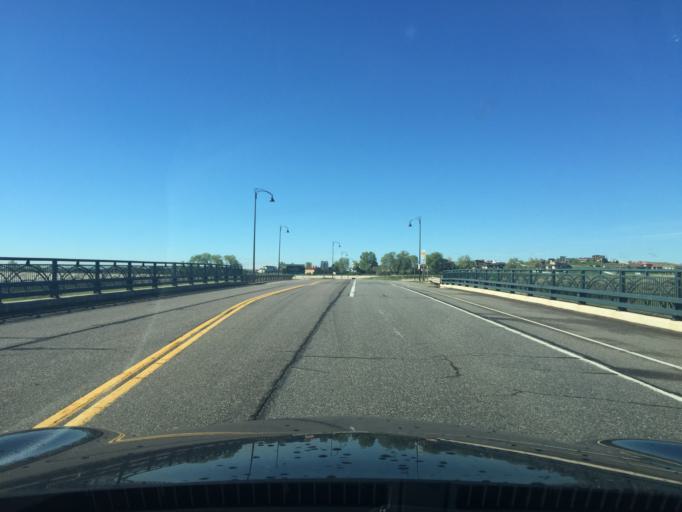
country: US
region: Colorado
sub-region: Boulder County
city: Lafayette
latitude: 39.9843
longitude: -105.0185
